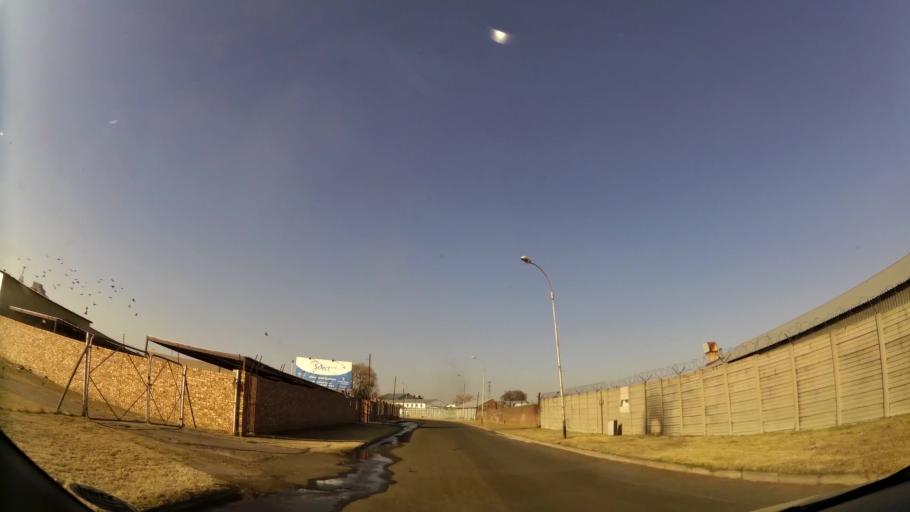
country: ZA
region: Gauteng
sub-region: West Rand District Municipality
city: Randfontein
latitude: -26.1916
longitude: 27.6897
